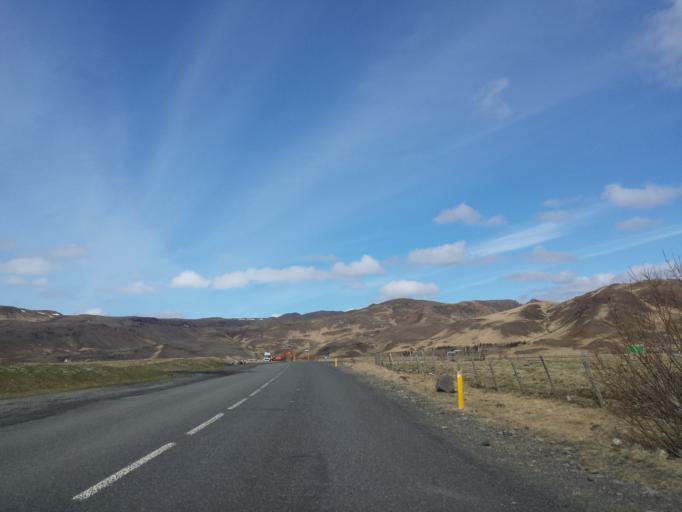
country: IS
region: South
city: Hveragerdi
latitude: 64.0104
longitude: -21.1905
